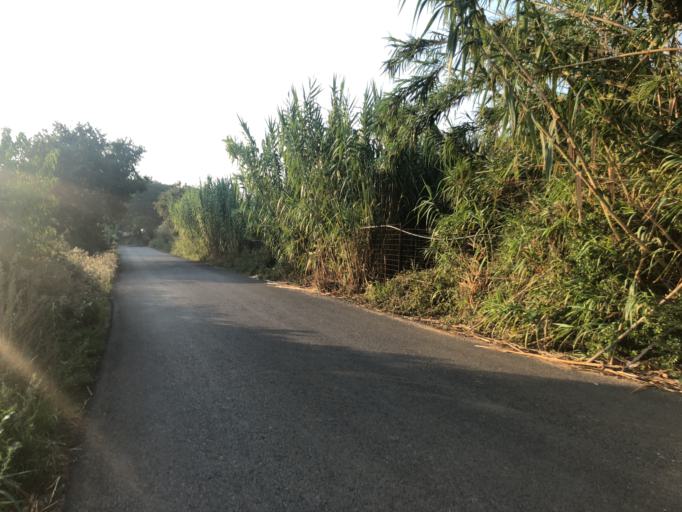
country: GR
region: Crete
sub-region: Nomos Chanias
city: Georgioupolis
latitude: 35.3502
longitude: 24.2792
